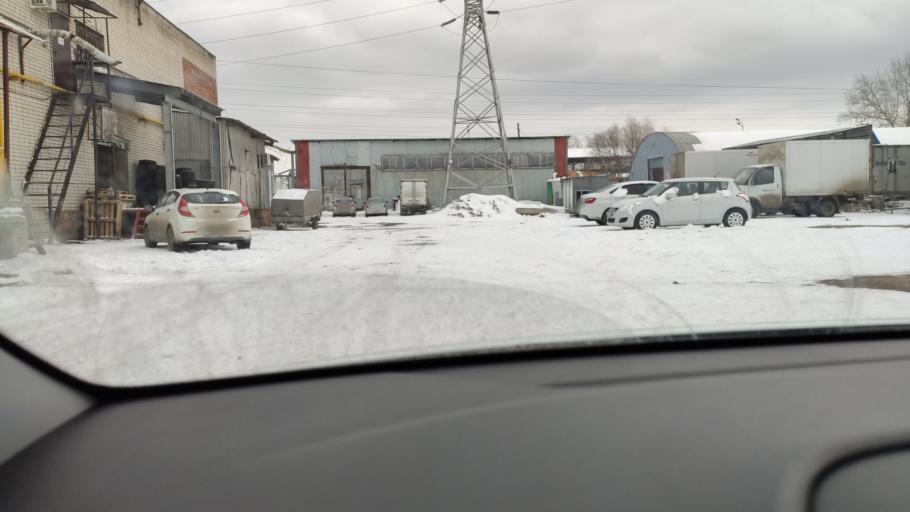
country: RU
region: Tatarstan
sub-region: Gorod Kazan'
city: Kazan
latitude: 55.7415
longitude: 49.1314
